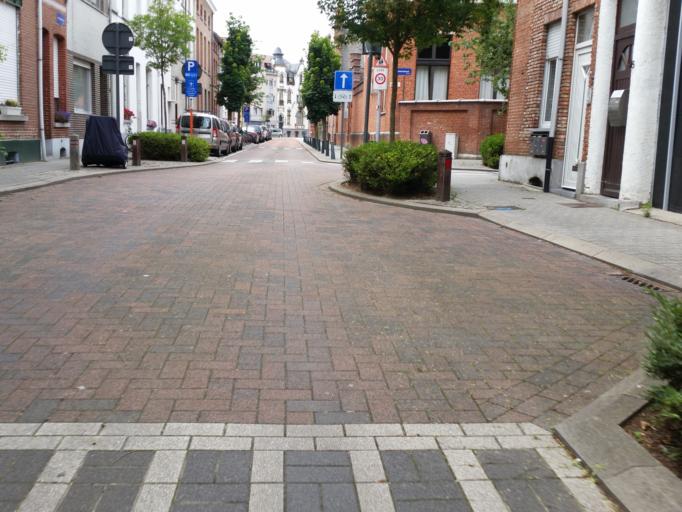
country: BE
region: Flanders
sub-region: Provincie Antwerpen
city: Mechelen
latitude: 51.0177
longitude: 4.4746
